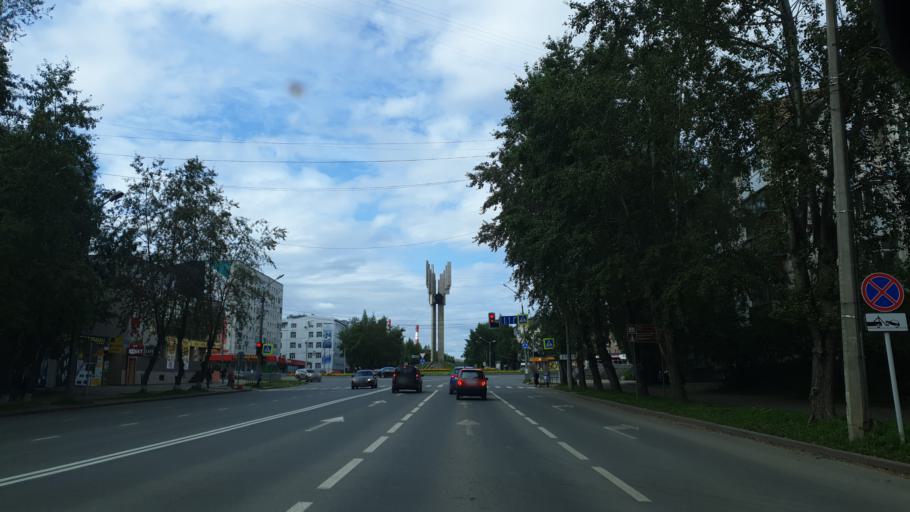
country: RU
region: Komi Republic
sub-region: Syktyvdinskiy Rayon
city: Syktyvkar
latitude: 61.6628
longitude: 50.8172
